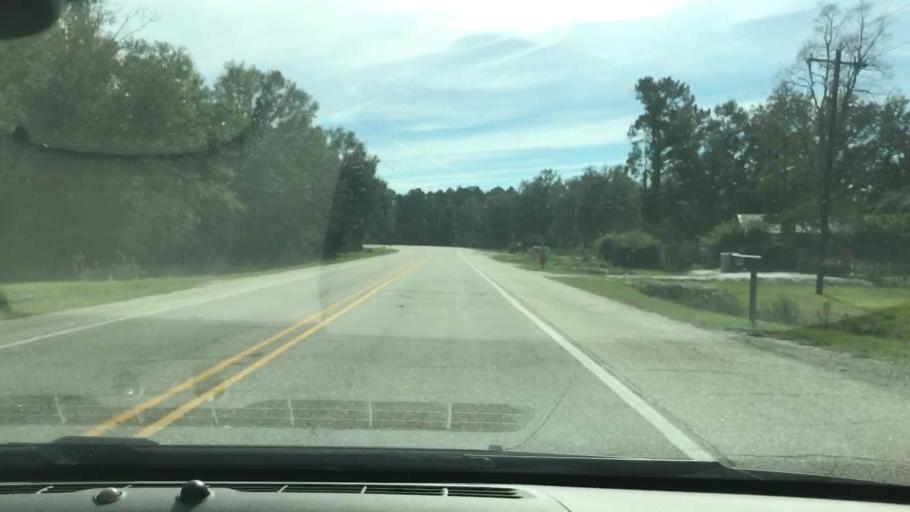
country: US
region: Louisiana
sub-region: Saint Tammany Parish
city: Pearl River
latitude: 30.4482
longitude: -89.7990
